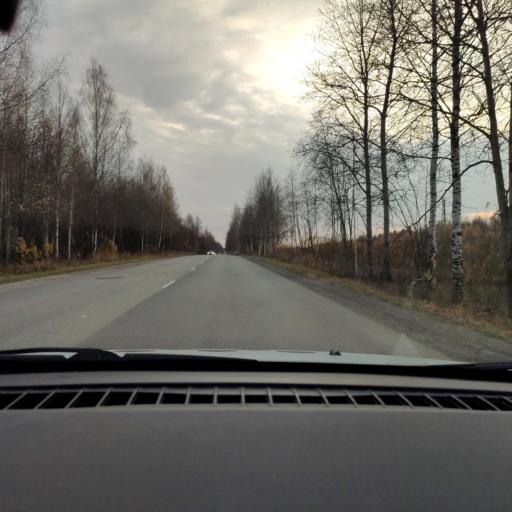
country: RU
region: Perm
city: Perm
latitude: 58.1034
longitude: 56.4145
